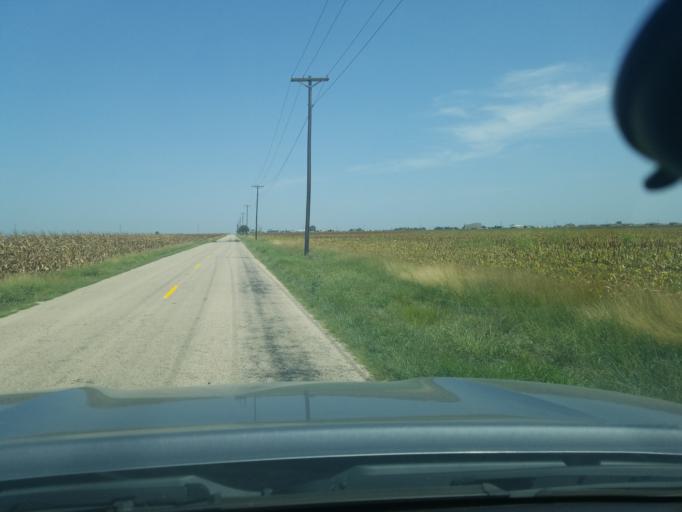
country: US
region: Texas
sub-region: Guadalupe County
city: Lake Dunlap
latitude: 29.6864
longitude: -98.0350
